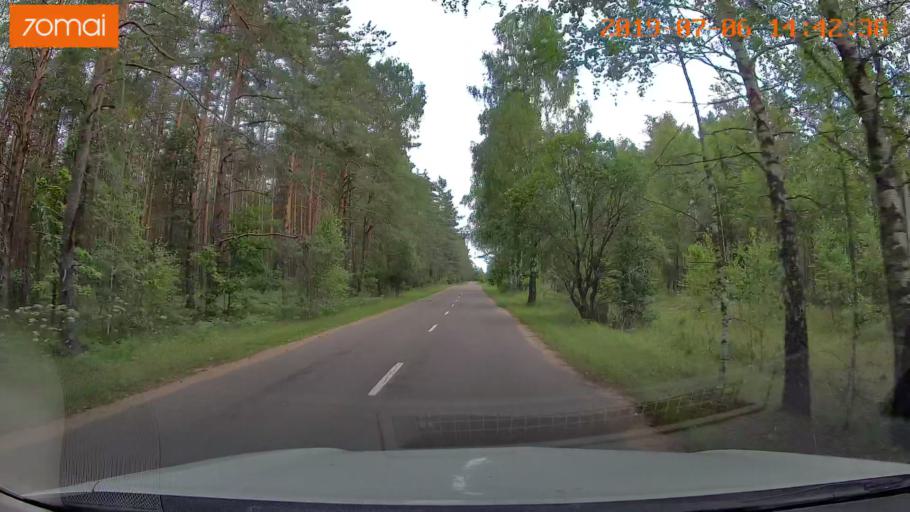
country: BY
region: Minsk
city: Ivyanyets
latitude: 53.9433
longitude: 26.6910
